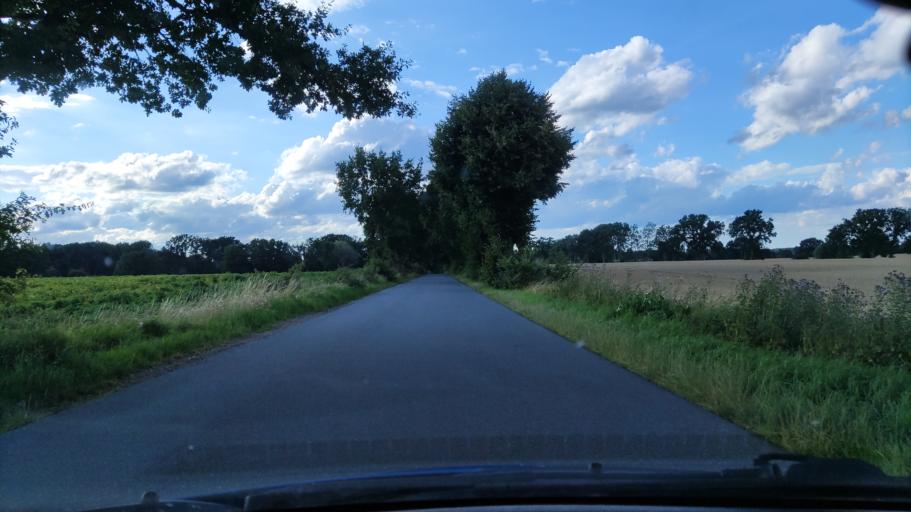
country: DE
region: Lower Saxony
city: Dahlenburg
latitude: 53.1746
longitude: 10.7002
